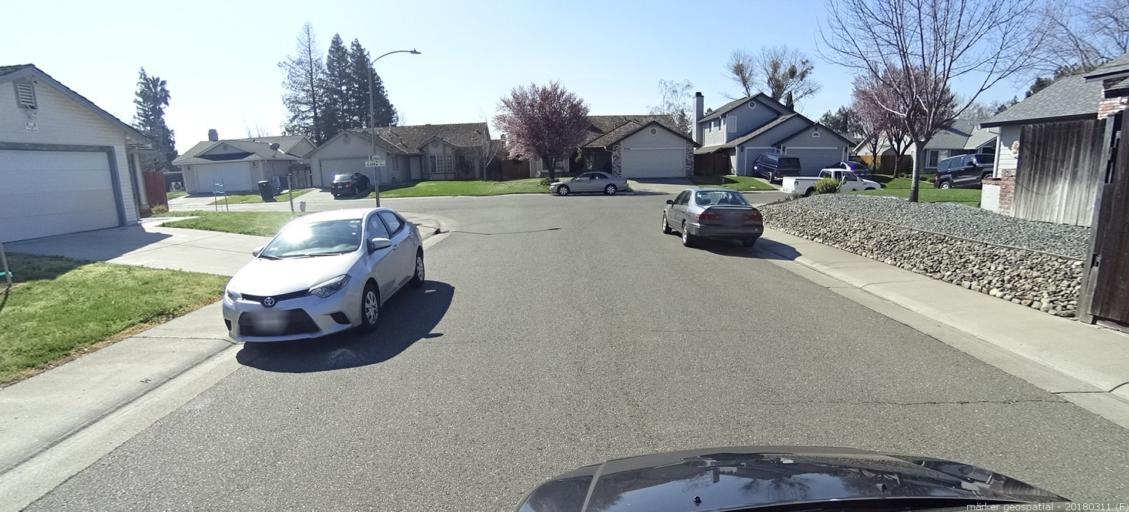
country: US
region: California
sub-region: Sacramento County
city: Florin
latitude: 38.4641
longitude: -121.4022
